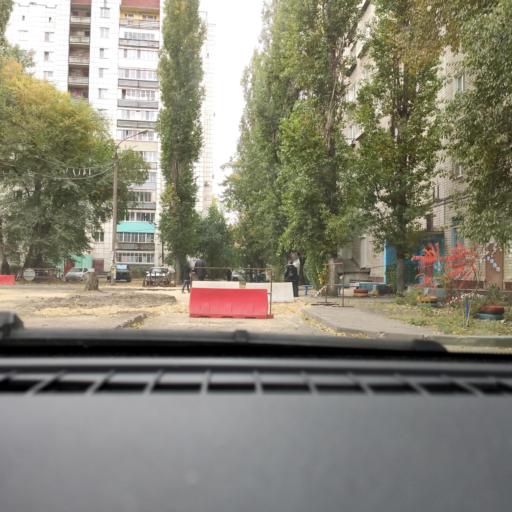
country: RU
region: Voronezj
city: Voronezh
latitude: 51.6388
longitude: 39.2674
